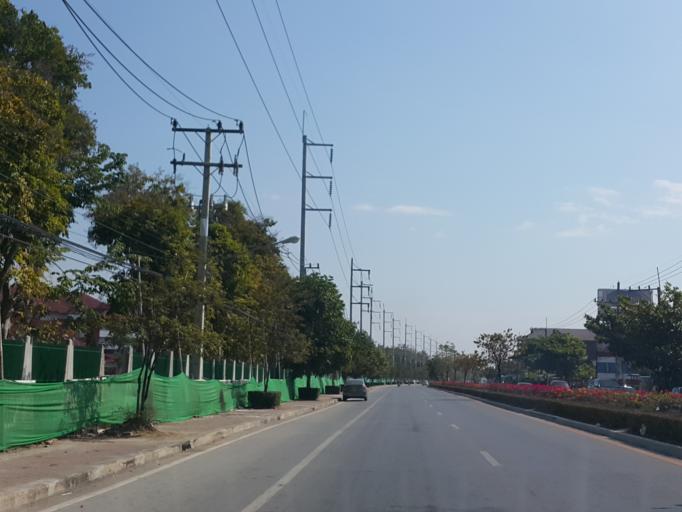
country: TH
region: Chiang Mai
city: San Sai
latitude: 18.8918
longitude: 99.0168
